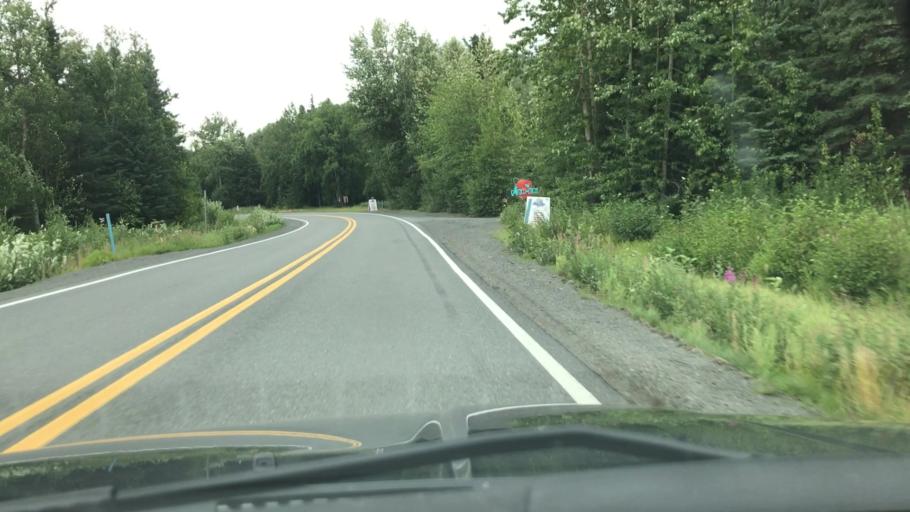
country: US
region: Alaska
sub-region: Kenai Peninsula Borough
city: Seward
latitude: 60.4880
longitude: -149.9768
